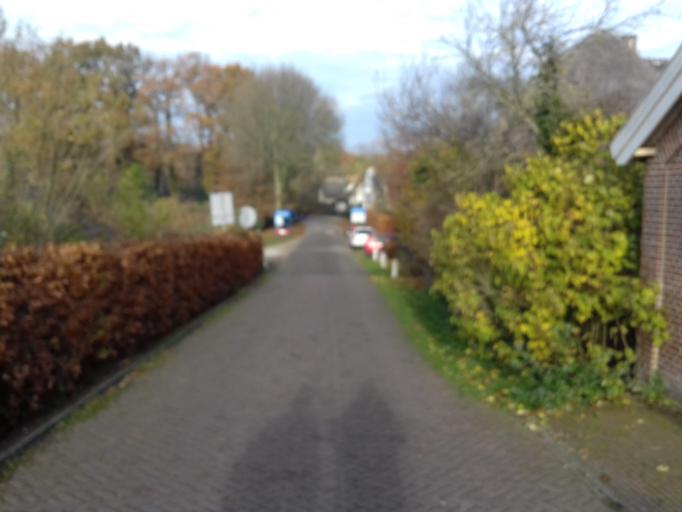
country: NL
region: Gelderland
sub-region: Gemeente Neerijnen
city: Neerijnen
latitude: 51.8273
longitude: 5.2815
